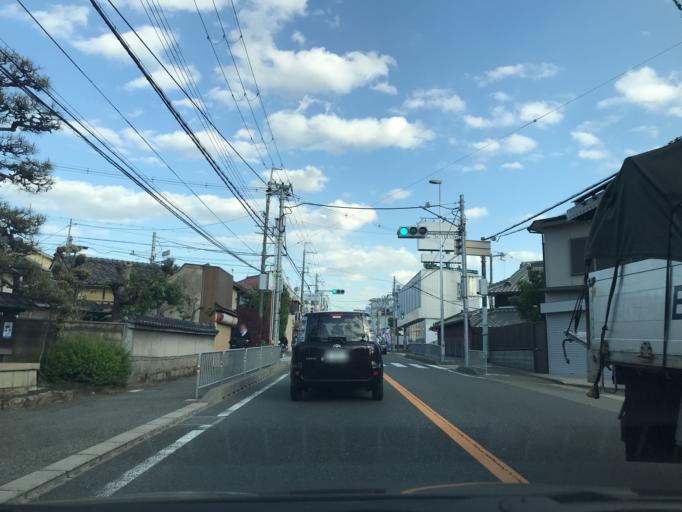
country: JP
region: Osaka
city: Ikeda
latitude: 34.8157
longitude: 135.4371
